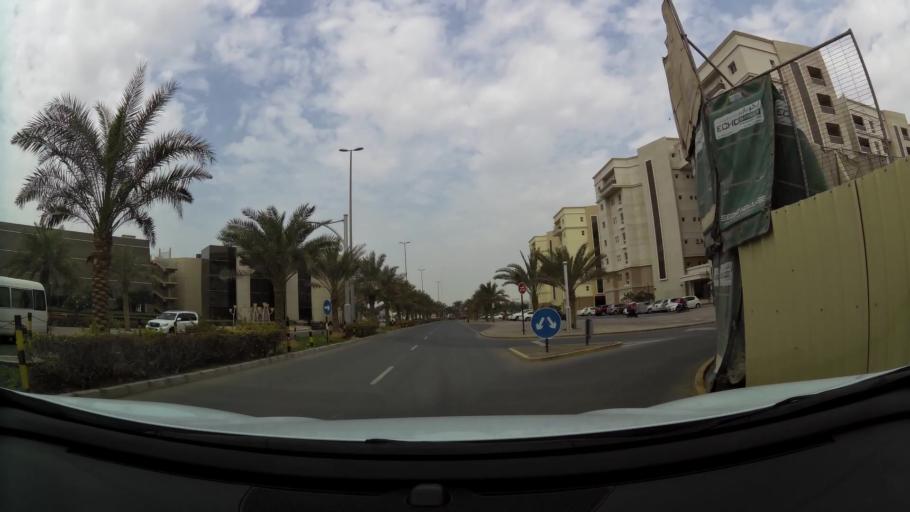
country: AE
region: Abu Dhabi
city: Abu Dhabi
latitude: 24.3134
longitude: 54.6215
